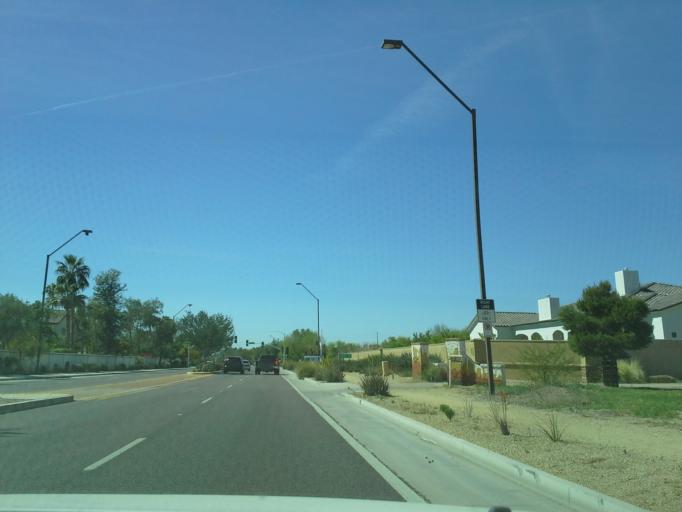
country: US
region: Arizona
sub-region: Maricopa County
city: Paradise Valley
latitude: 33.5971
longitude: -111.8851
